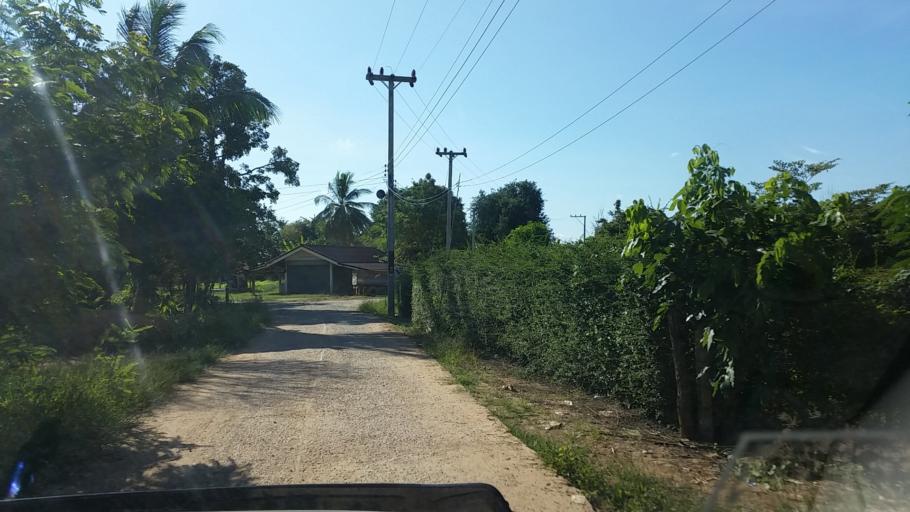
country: TH
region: Chaiyaphum
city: Thep Sathit
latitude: 15.5467
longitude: 101.4789
